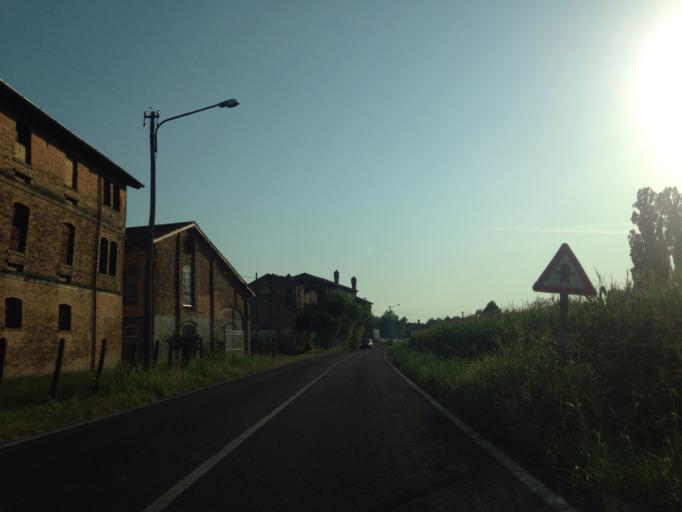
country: IT
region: Veneto
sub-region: Provincia di Venezia
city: Fossalta di Portogruaro
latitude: 45.7569
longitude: 12.9232
